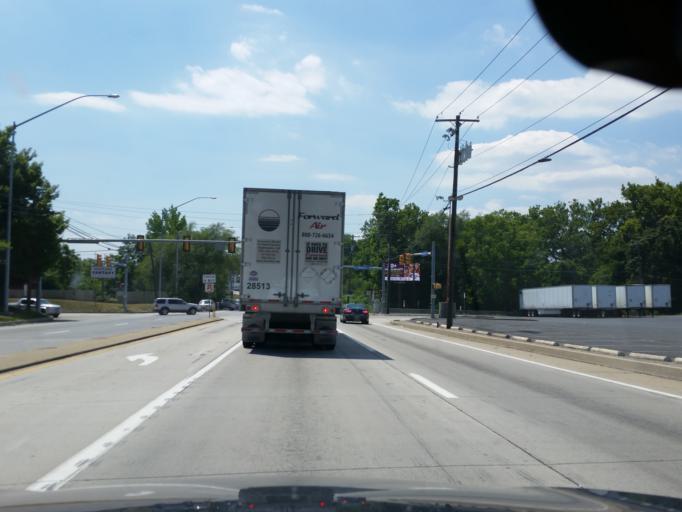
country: US
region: Pennsylvania
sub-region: Cumberland County
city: Schlusser
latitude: 40.2343
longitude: -77.1371
